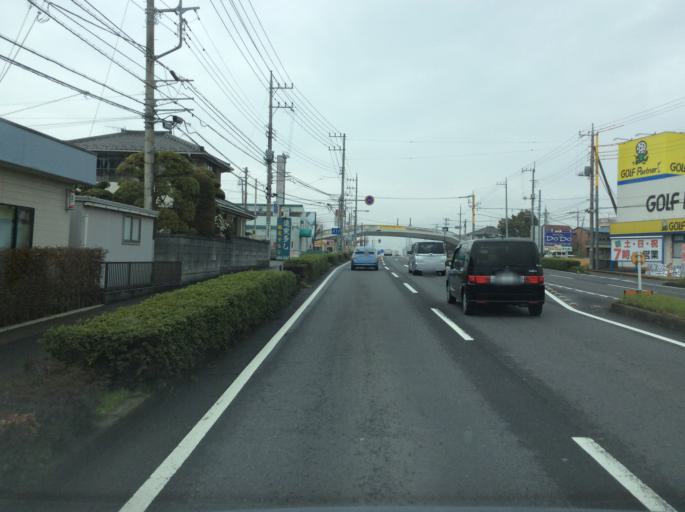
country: JP
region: Ibaraki
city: Mitsukaido
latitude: 35.9792
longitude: 139.9822
